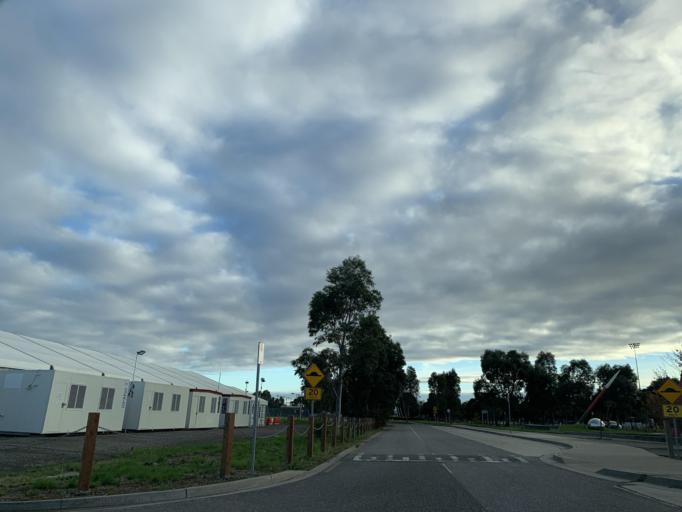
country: AU
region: Victoria
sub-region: Casey
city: Cranbourne East
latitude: -38.1215
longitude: 145.3077
